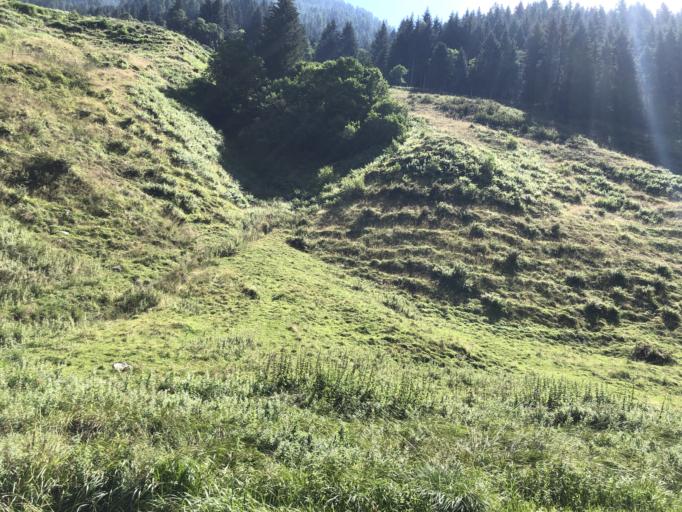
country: AT
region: Tyrol
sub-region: Politischer Bezirk Kitzbuhel
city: Kirchberg in Tirol
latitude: 47.3592
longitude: 12.2906
